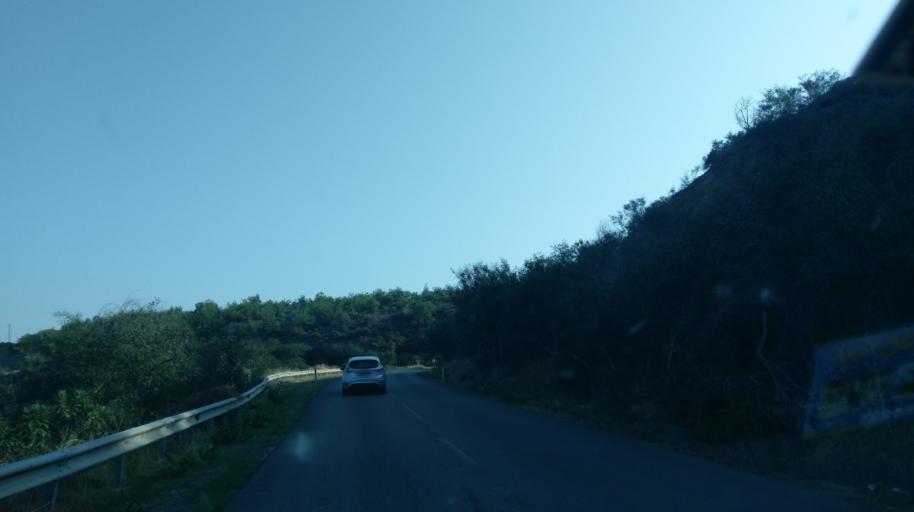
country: CY
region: Lefkosia
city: Lefka
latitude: 35.1531
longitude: 32.7926
